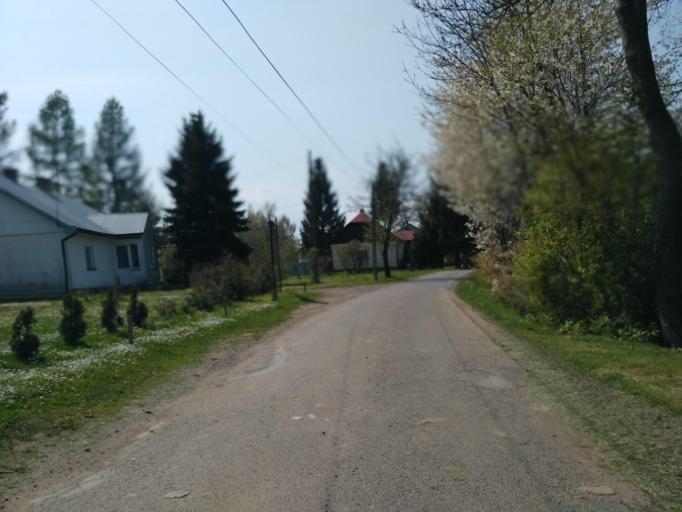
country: PL
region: Subcarpathian Voivodeship
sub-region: Powiat krosnienski
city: Chorkowka
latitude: 49.6448
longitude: 21.7236
